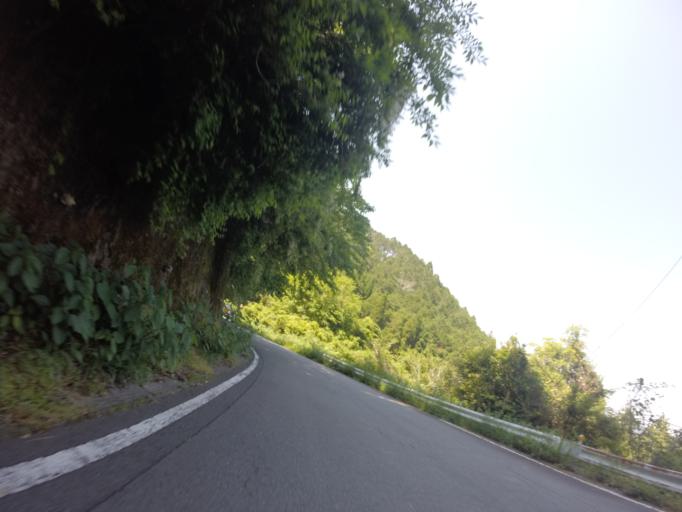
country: JP
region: Shizuoka
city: Fujinomiya
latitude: 35.1601
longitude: 138.5711
